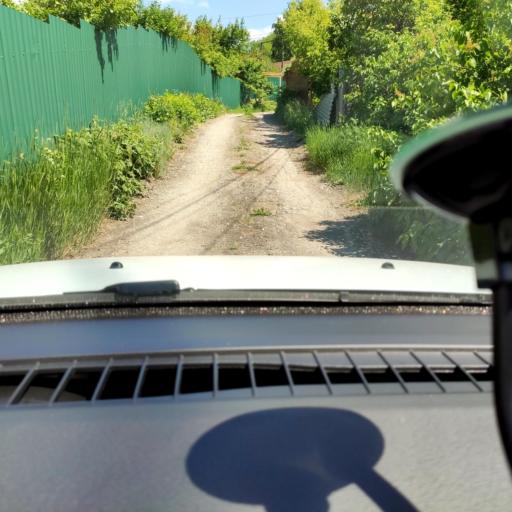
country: RU
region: Samara
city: Samara
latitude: 53.1762
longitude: 50.1605
